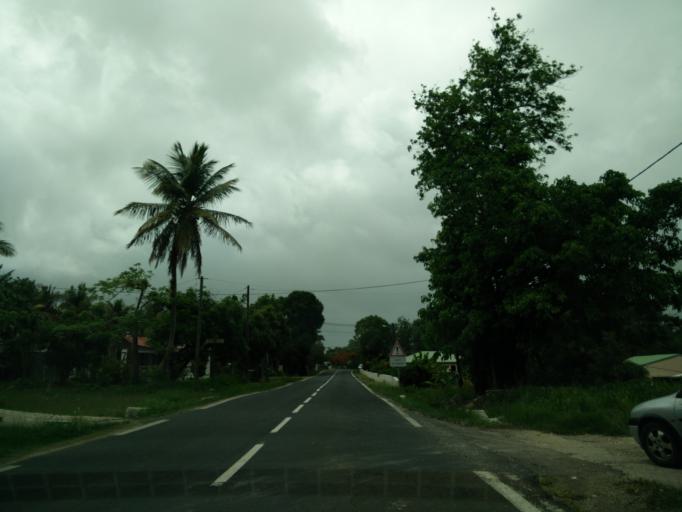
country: GP
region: Guadeloupe
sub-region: Guadeloupe
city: Grand-Bourg
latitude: 15.9070
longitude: -61.2623
